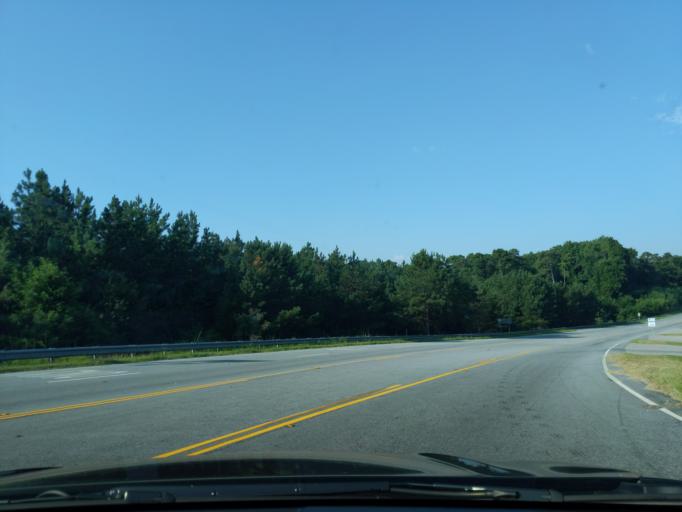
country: US
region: South Carolina
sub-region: Newberry County
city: Newberry
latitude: 34.3105
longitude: -81.5753
